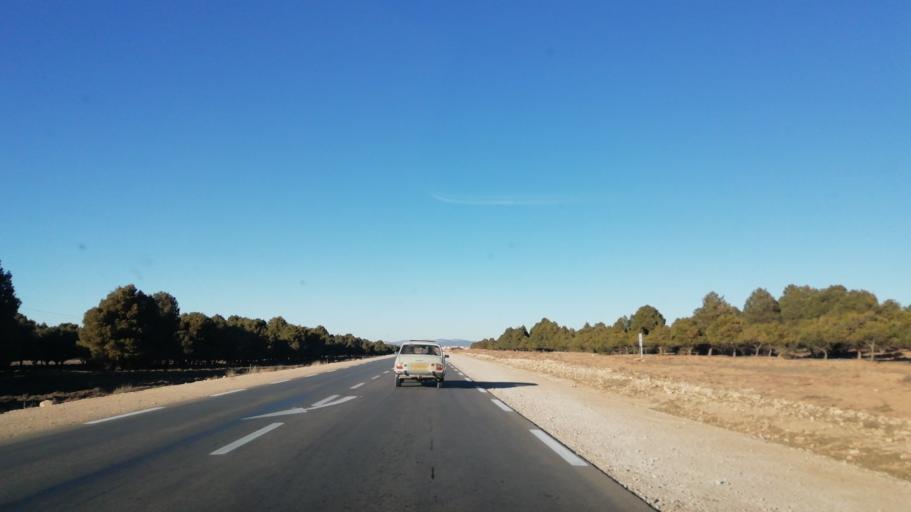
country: DZ
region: Tlemcen
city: Sebdou
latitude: 34.4622
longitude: -1.2749
